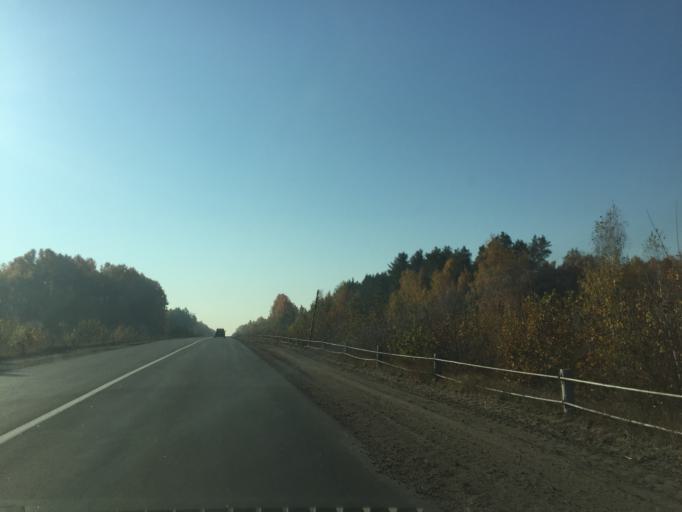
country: BY
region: Gomel
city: Gomel
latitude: 52.4201
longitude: 30.8284
